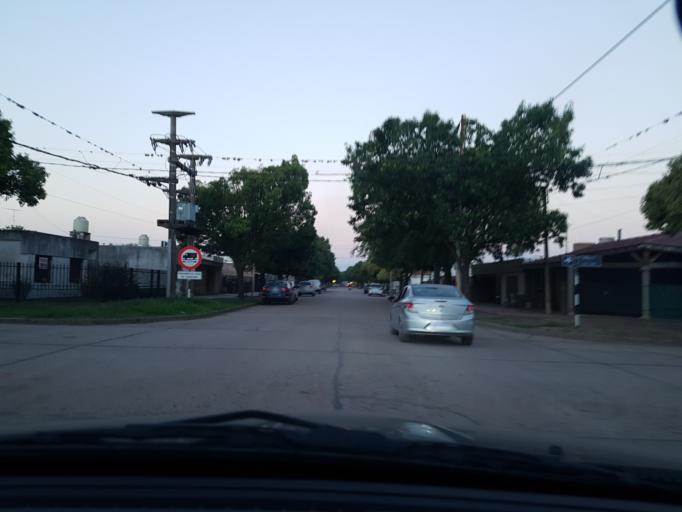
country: AR
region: Cordoba
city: General Cabrera
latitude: -32.7590
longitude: -63.7960
